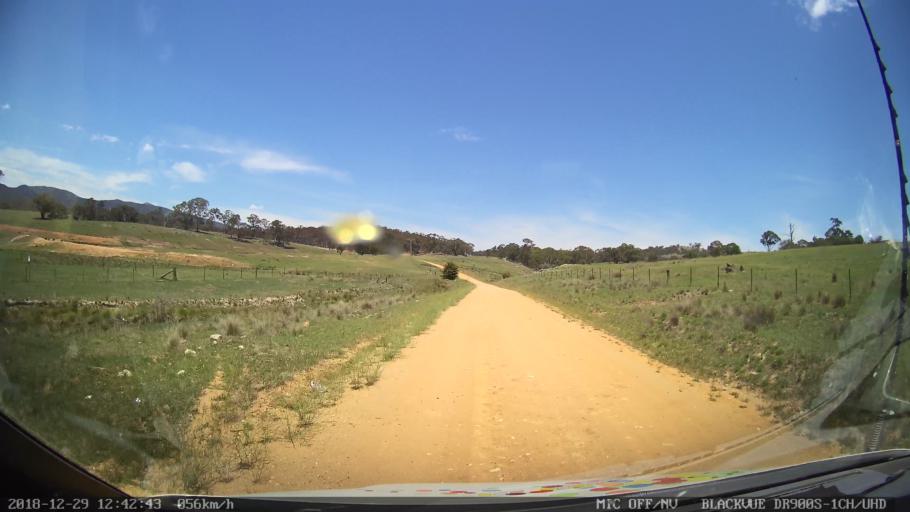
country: AU
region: Australian Capital Territory
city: Macarthur
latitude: -35.6150
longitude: 149.2188
